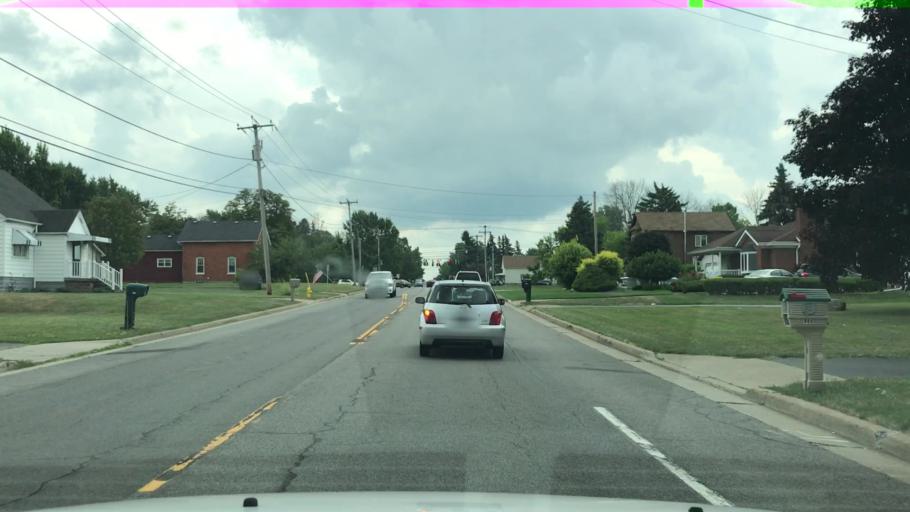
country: US
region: New York
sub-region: Erie County
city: Depew
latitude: 42.8817
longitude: -78.7091
